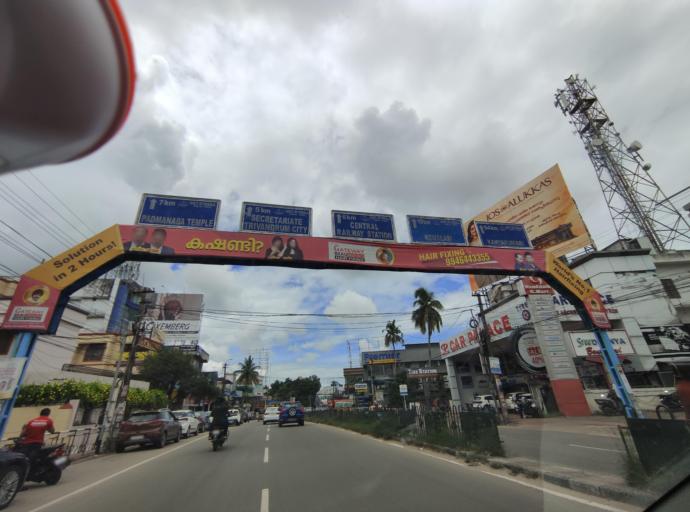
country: IN
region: Kerala
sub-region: Thiruvananthapuram
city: Thiruvananthapuram
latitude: 8.5284
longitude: 76.9389
